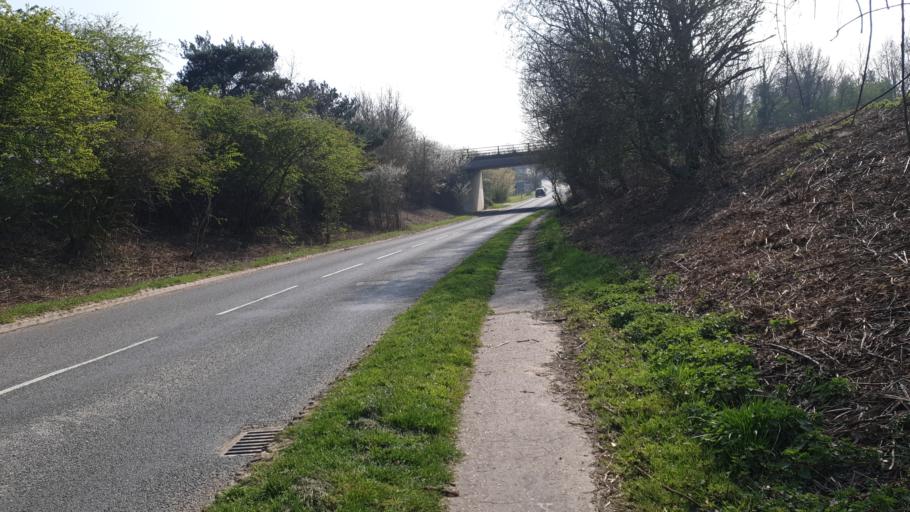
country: GB
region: England
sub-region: Essex
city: Mistley
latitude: 51.9146
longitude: 1.1434
